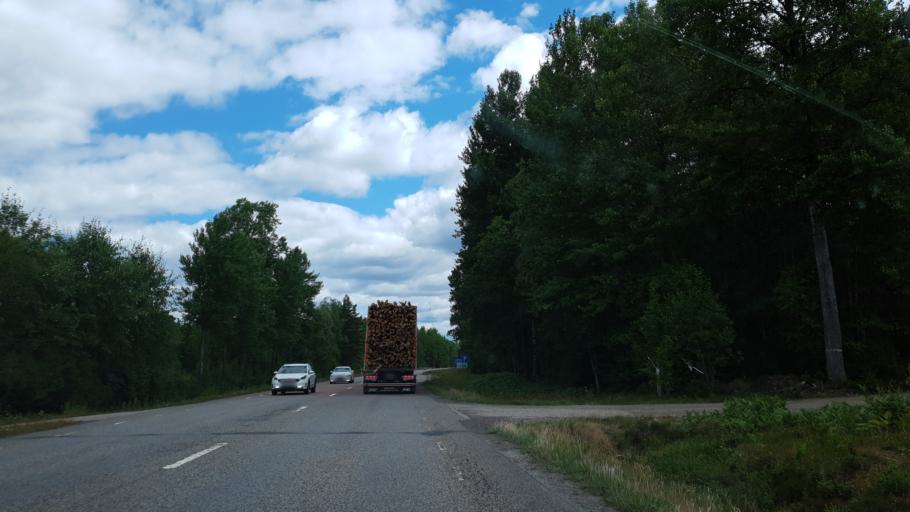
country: SE
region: Kronoberg
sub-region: Uppvidinge Kommun
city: Aseda
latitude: 57.1553
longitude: 15.3196
